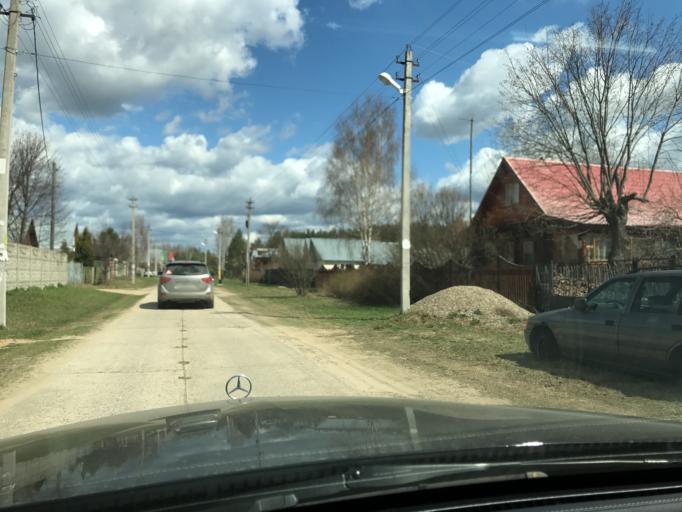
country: RU
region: Vladimir
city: Pokrov
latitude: 55.8560
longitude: 39.2008
